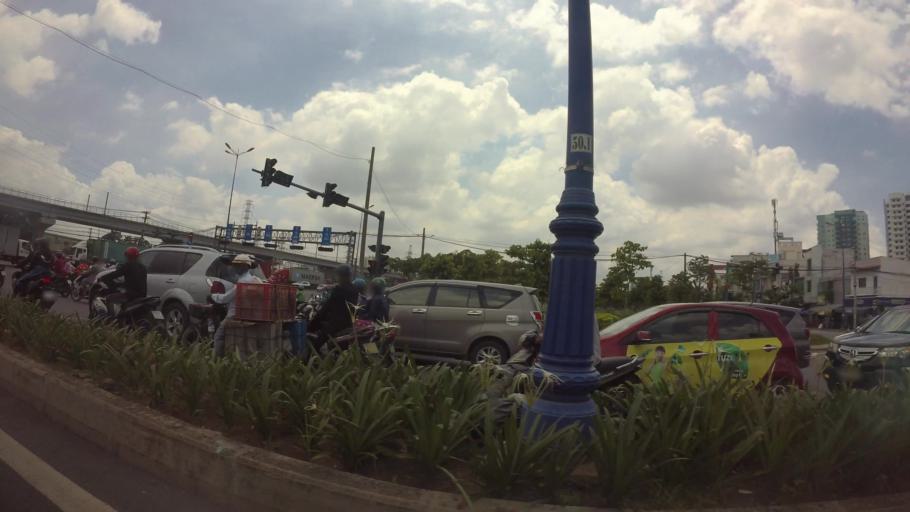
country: VN
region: Ho Chi Minh City
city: Quan Chin
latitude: 10.8282
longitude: 106.7627
